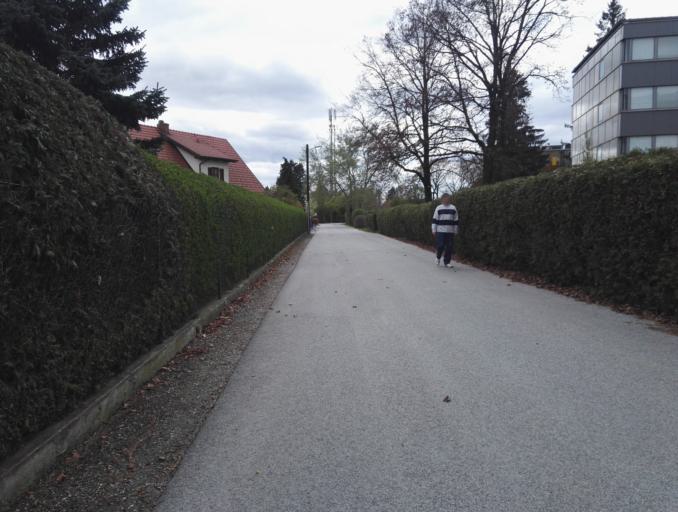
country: AT
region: Styria
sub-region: Politischer Bezirk Graz-Umgebung
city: Feldkirchen bei Graz
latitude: 47.0379
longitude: 15.4659
